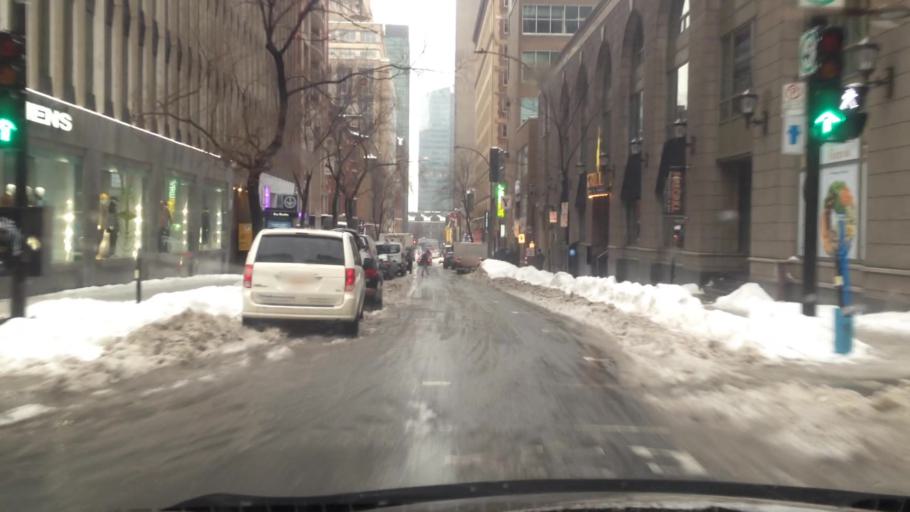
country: CA
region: Quebec
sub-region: Montreal
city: Montreal
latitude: 45.5003
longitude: -73.5755
